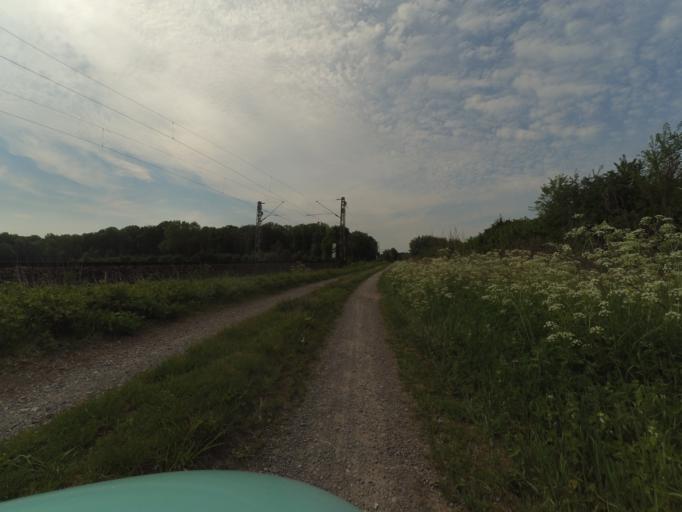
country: DE
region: Lower Saxony
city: Sehnde
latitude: 52.3408
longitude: 9.9676
